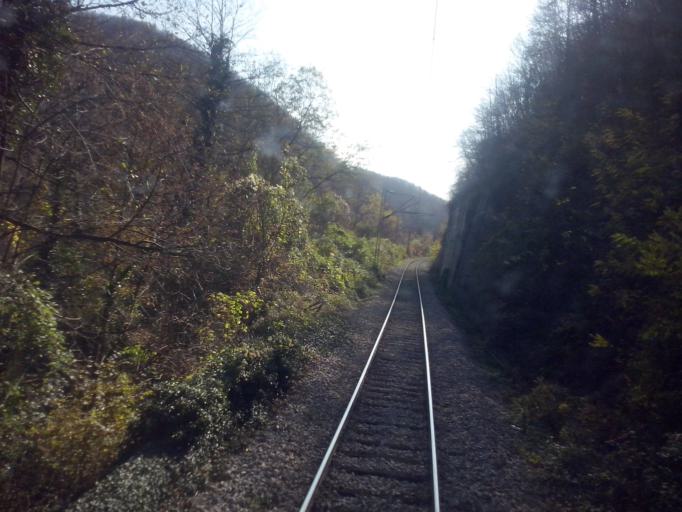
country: RS
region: Central Serbia
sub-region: Zlatiborski Okrug
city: Kosjeric
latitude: 43.9538
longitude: 19.9819
